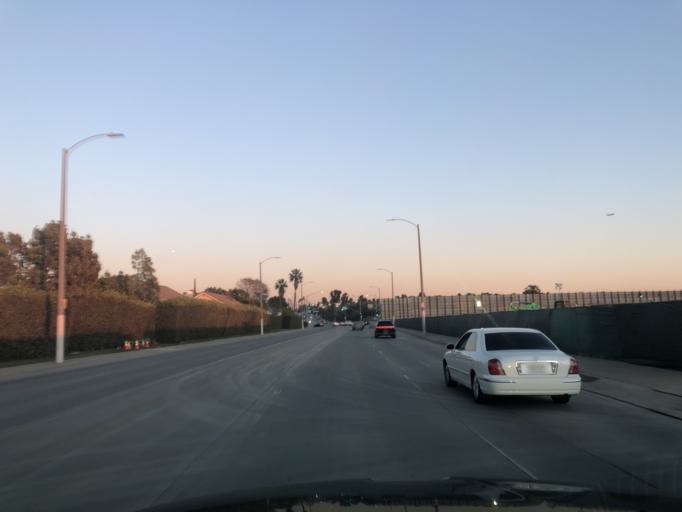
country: US
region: California
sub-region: Los Angeles County
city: Inglewood
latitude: 33.9564
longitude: -118.3377
